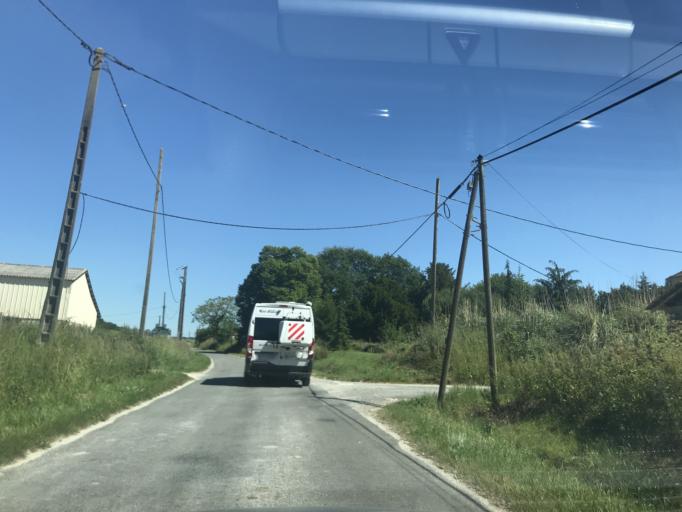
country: FR
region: Poitou-Charentes
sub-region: Departement de la Charente-Maritime
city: Mortagne-sur-Gironde
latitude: 45.4250
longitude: -0.7262
